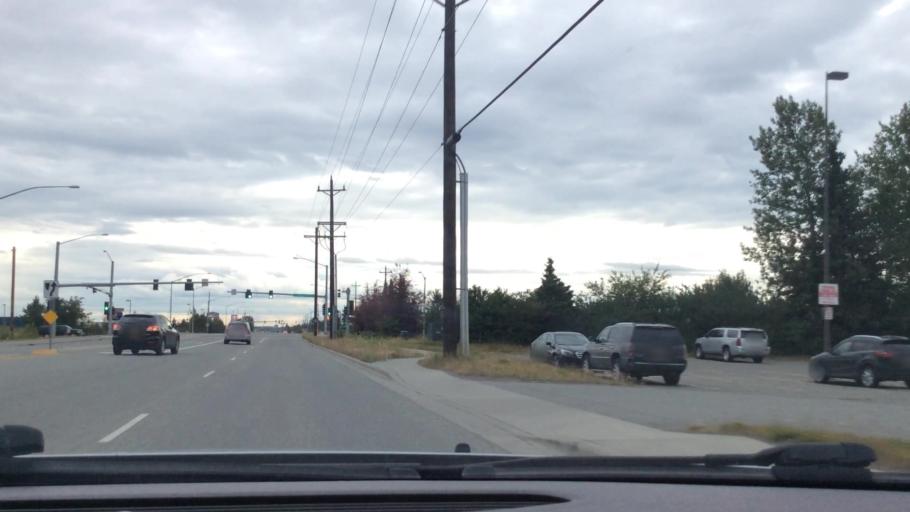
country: US
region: Alaska
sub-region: Anchorage Municipality
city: Anchorage
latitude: 61.1184
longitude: -149.8638
